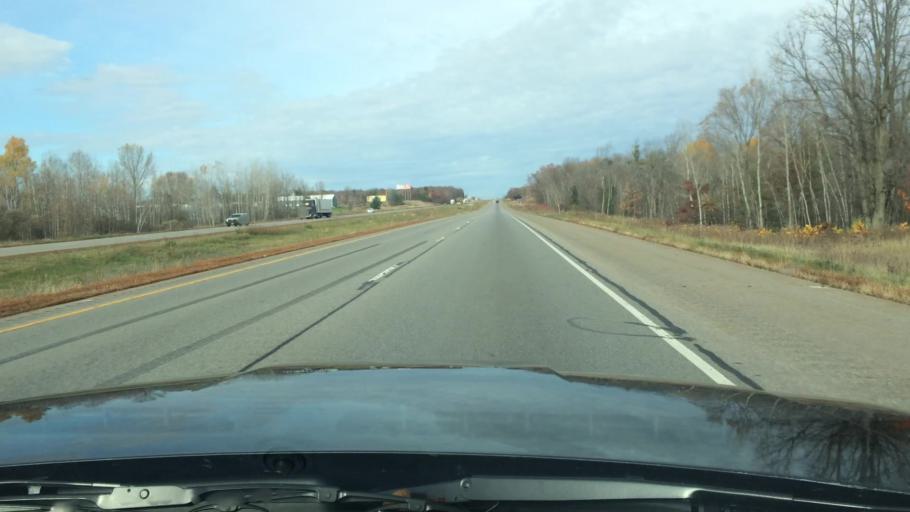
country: US
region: Wisconsin
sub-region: Marathon County
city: Mosinee
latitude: 44.7526
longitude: -89.6798
